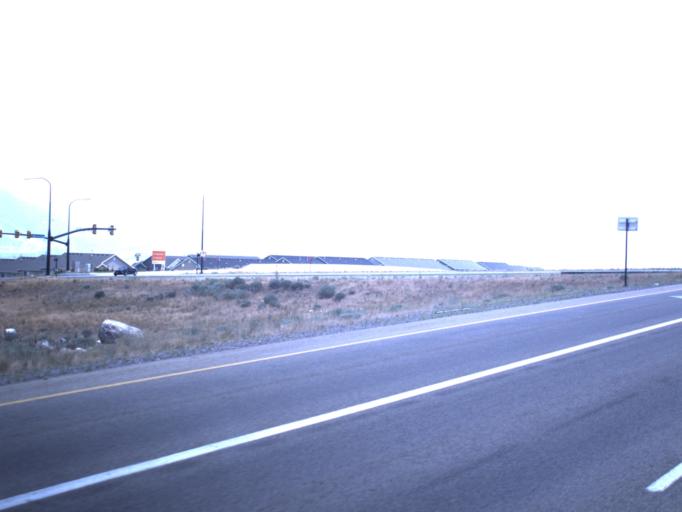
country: US
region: Utah
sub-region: Salt Lake County
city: Herriman
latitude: 40.4892
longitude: -112.0011
